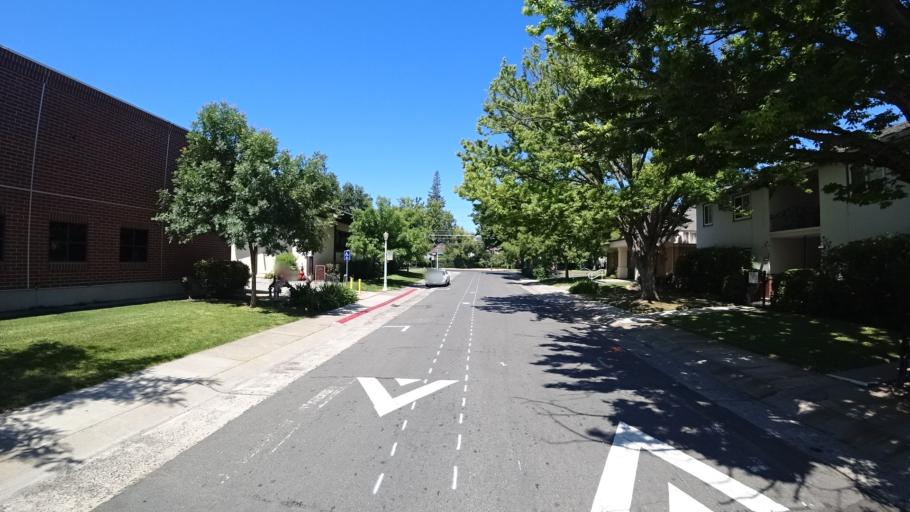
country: US
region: California
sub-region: Sacramento County
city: Sacramento
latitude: 38.5427
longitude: -121.4905
